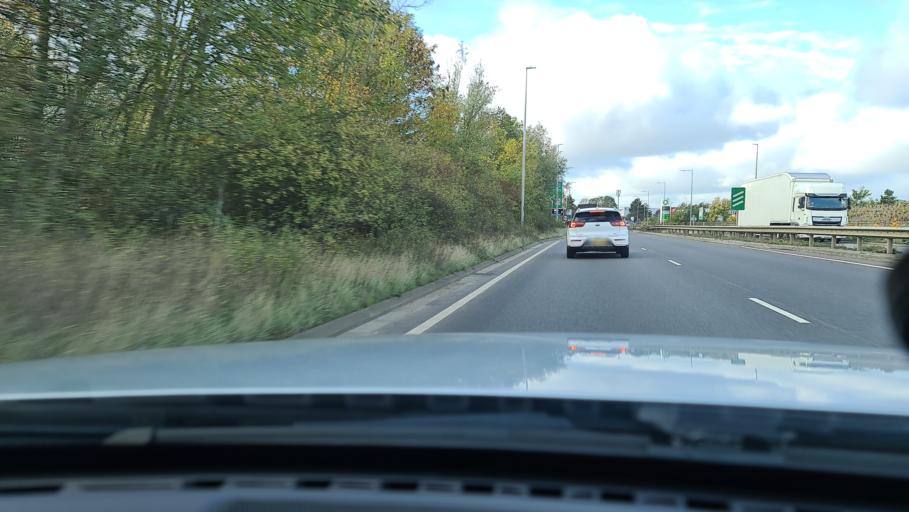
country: GB
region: England
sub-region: Milton Keynes
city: Wavendon
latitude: 52.0332
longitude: -0.6742
